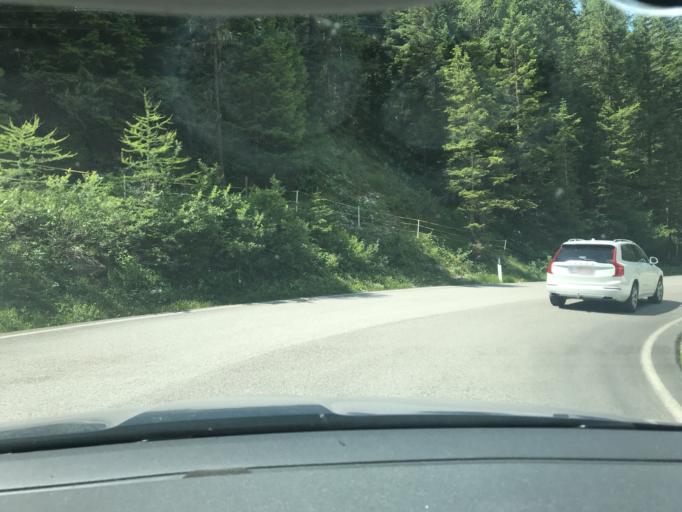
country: IT
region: Veneto
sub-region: Provincia di Belluno
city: Cortina d'Ampezzo
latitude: 46.5974
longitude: 12.2420
